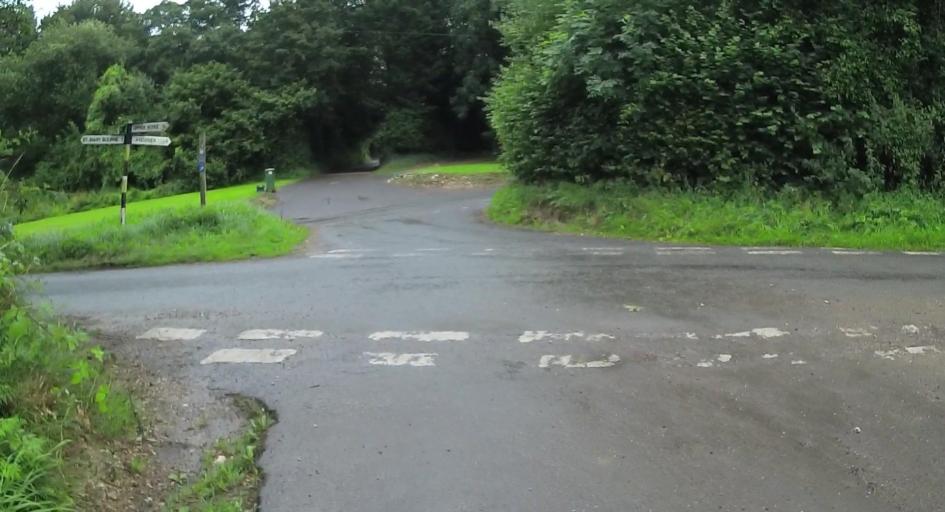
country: GB
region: England
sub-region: Hampshire
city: Andover
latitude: 51.2488
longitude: -1.4112
